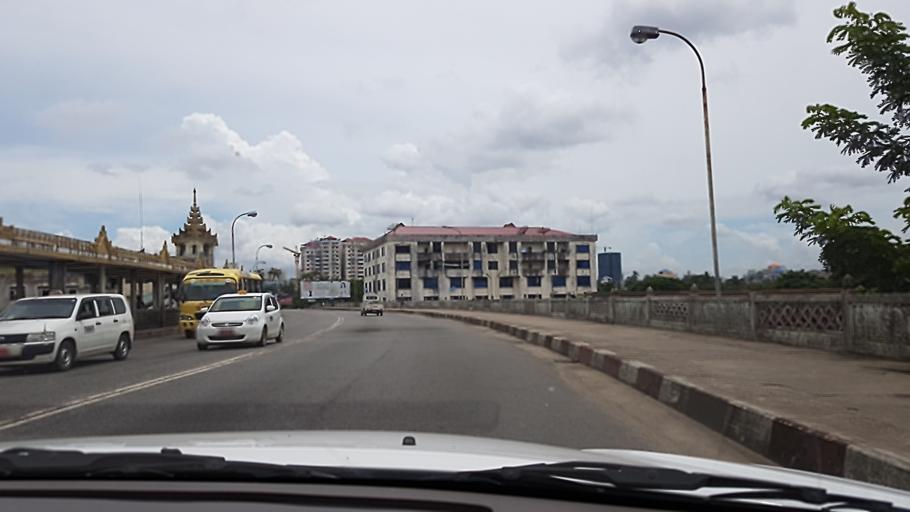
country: MM
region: Yangon
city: Yangon
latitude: 16.7802
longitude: 96.1622
